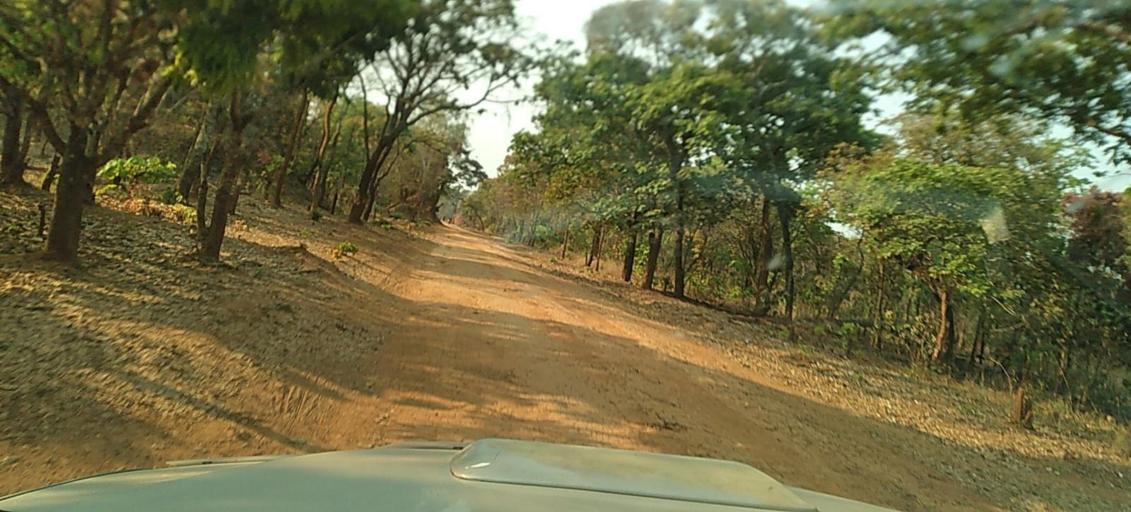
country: ZM
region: North-Western
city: Kasempa
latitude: -13.2881
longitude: 26.5551
